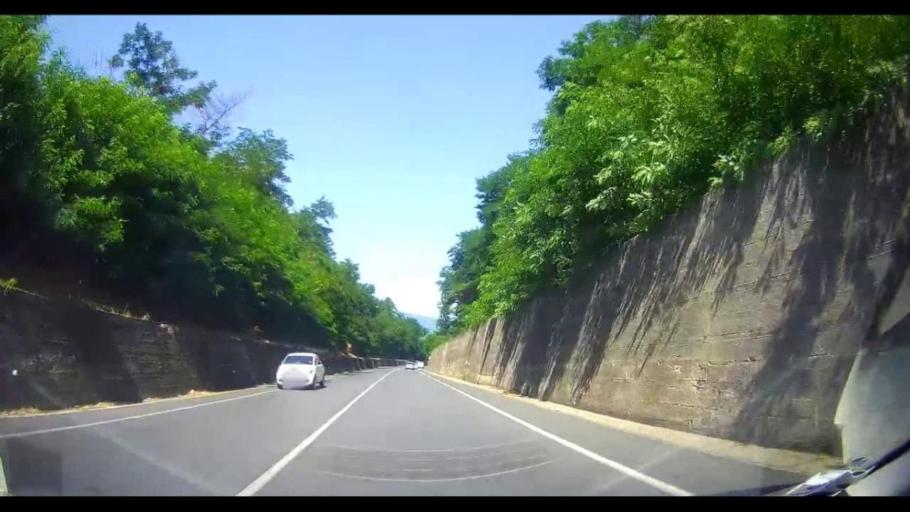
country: IT
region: Calabria
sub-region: Provincia di Cosenza
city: Zumpano
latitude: 39.2983
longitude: 16.2951
